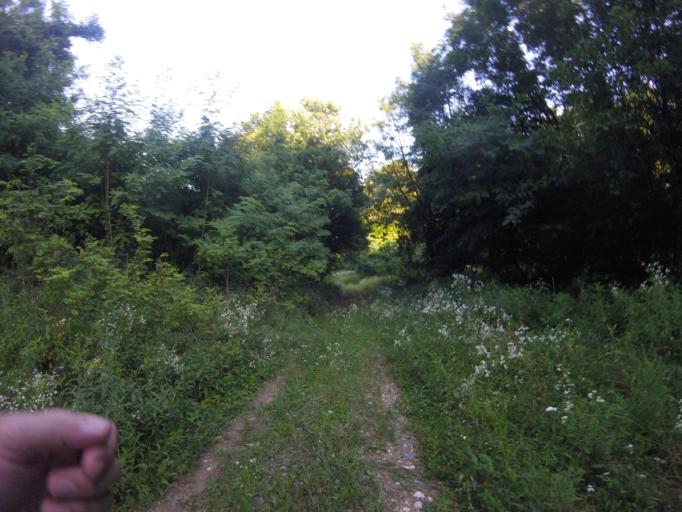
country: HU
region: Zala
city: Letenye
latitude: 46.5165
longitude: 16.7219
